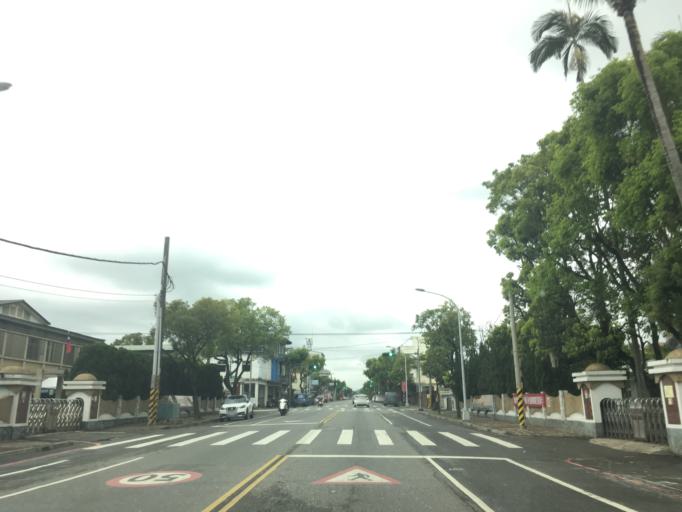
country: TW
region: Taiwan
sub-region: Hualien
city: Hualian
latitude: 23.9752
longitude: 121.5643
